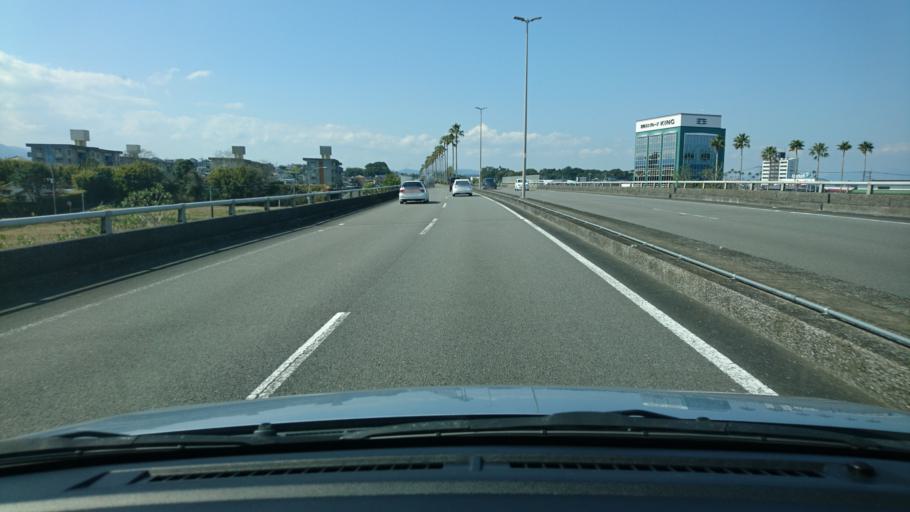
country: JP
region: Miyazaki
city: Miyazaki-shi
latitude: 31.8667
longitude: 131.4380
